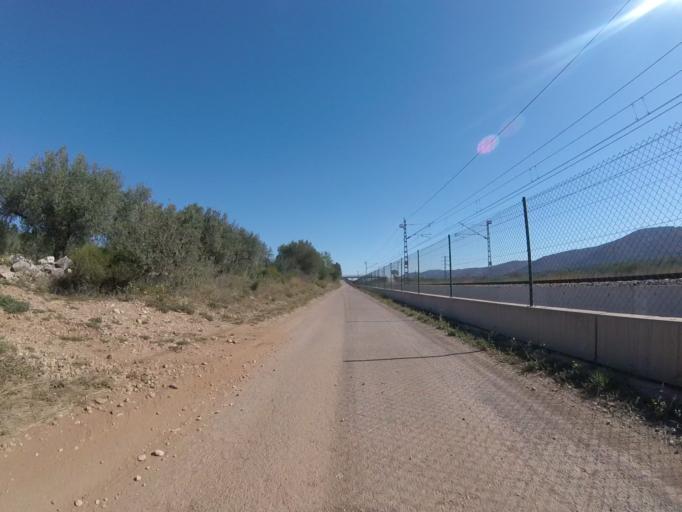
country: ES
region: Valencia
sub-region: Provincia de Castello
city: Santa Magdalena de Pulpis
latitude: 40.3461
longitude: 0.2714
